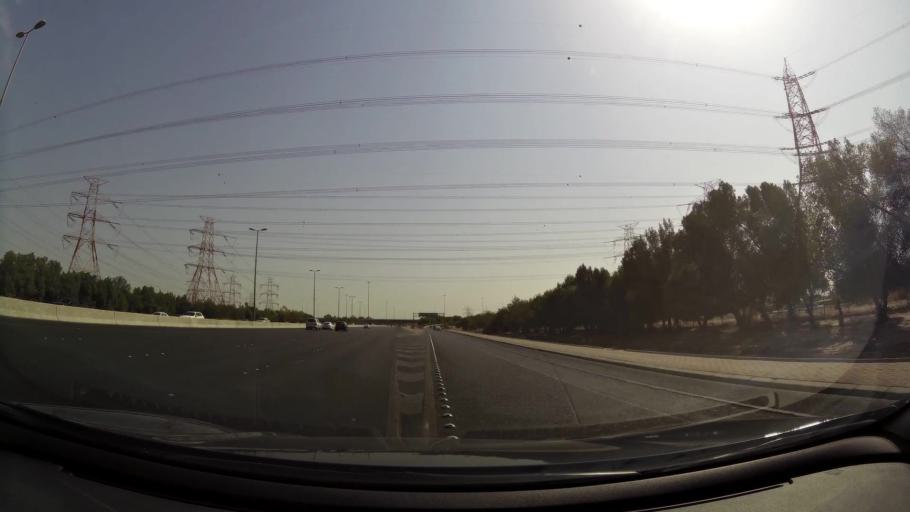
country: KW
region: Mubarak al Kabir
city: Sabah as Salim
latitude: 29.2711
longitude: 48.0393
